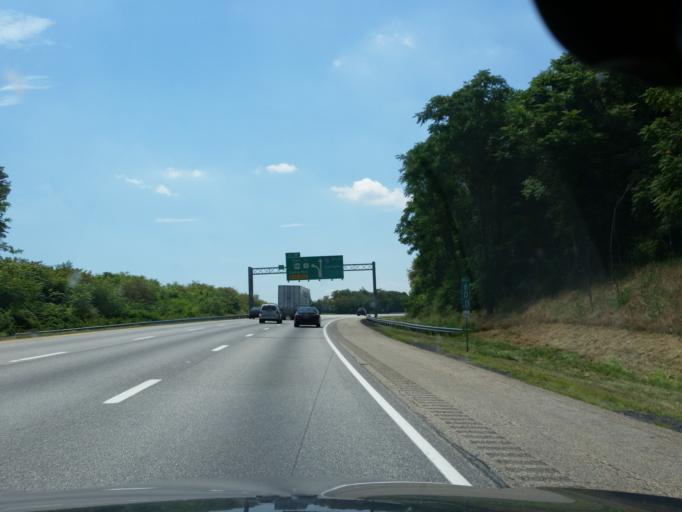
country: US
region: Pennsylvania
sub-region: Cumberland County
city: Enola
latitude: 40.2772
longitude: -76.9880
